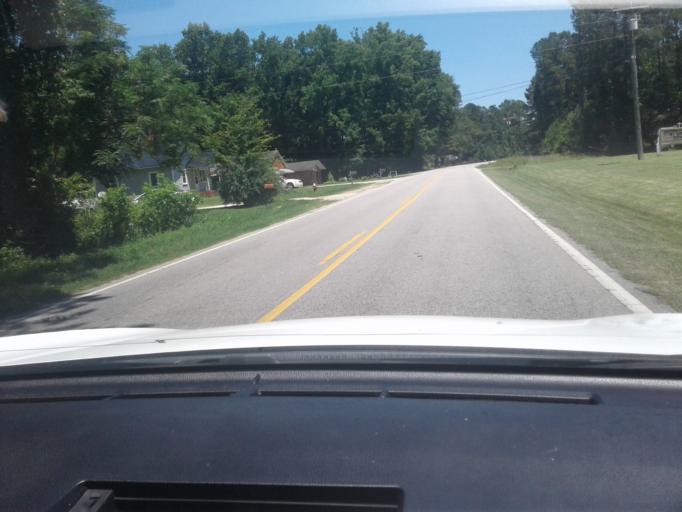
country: US
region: North Carolina
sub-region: Harnett County
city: Erwin
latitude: 35.3176
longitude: -78.7107
